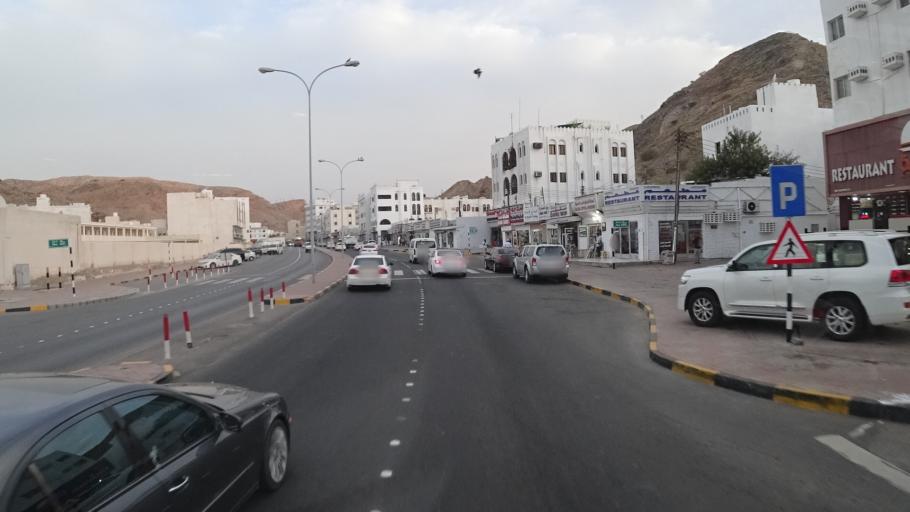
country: OM
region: Muhafazat Masqat
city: Muscat
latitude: 23.5841
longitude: 58.5403
